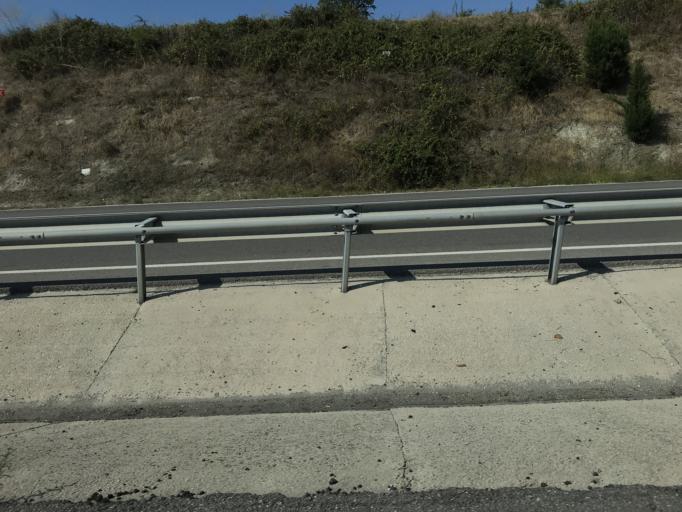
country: TR
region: Bursa
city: Mahmudiye
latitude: 40.2083
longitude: 28.5969
